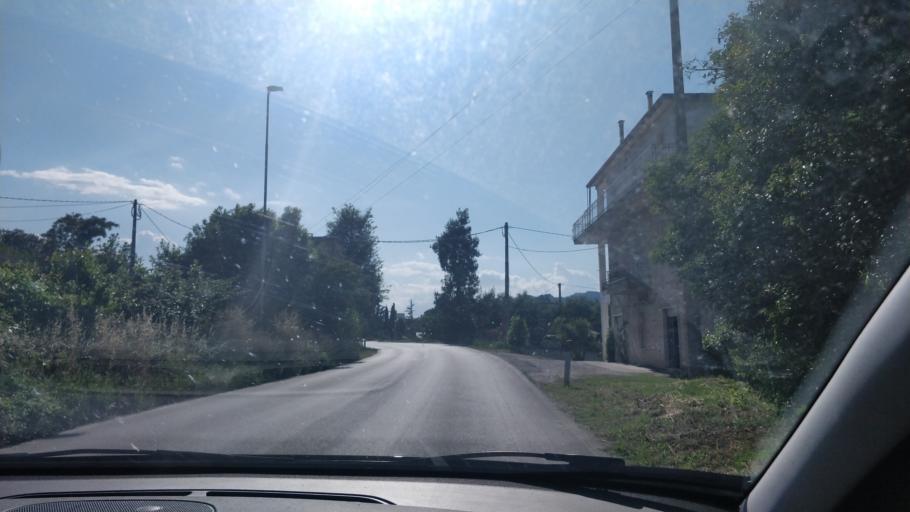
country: IT
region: The Marches
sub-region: Provincia di Ascoli Piceno
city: Massignano
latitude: 43.0364
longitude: 13.8276
